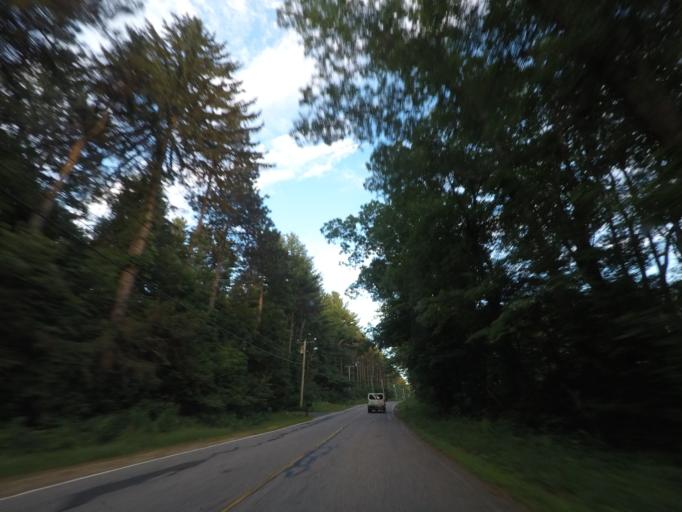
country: US
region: Massachusetts
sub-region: Worcester County
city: Warren
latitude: 42.1821
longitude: -72.1639
